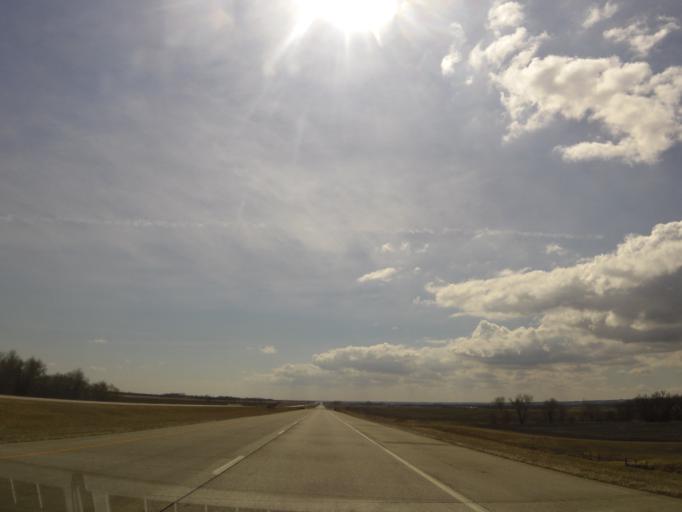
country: US
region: South Dakota
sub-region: Roberts County
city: Sisseton
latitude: 45.5880
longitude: -96.9896
